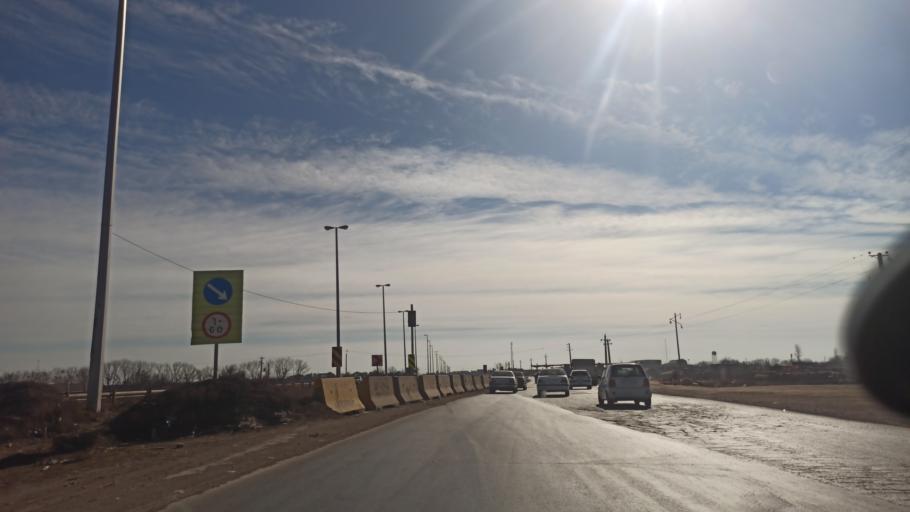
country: IR
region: Qazvin
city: Alvand
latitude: 36.1992
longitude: 50.0142
